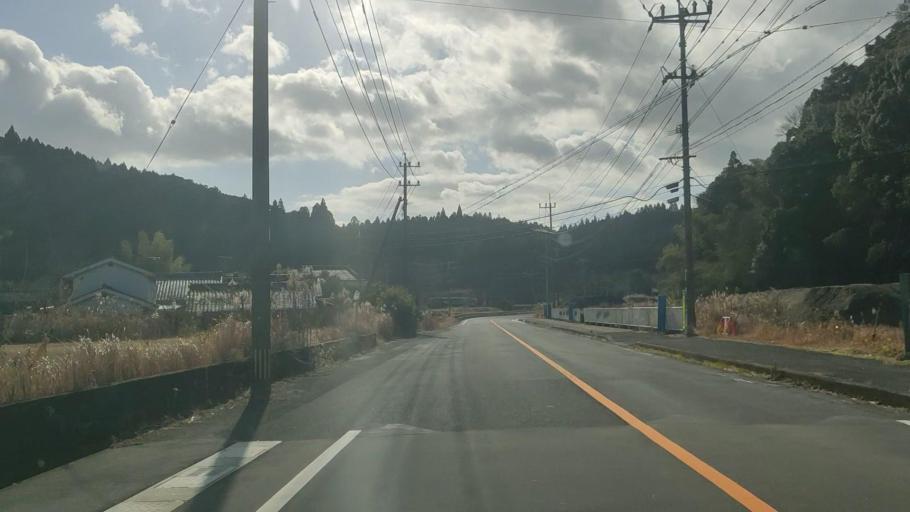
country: JP
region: Kagoshima
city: Okuchi-shinohara
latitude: 31.9409
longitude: 130.7095
